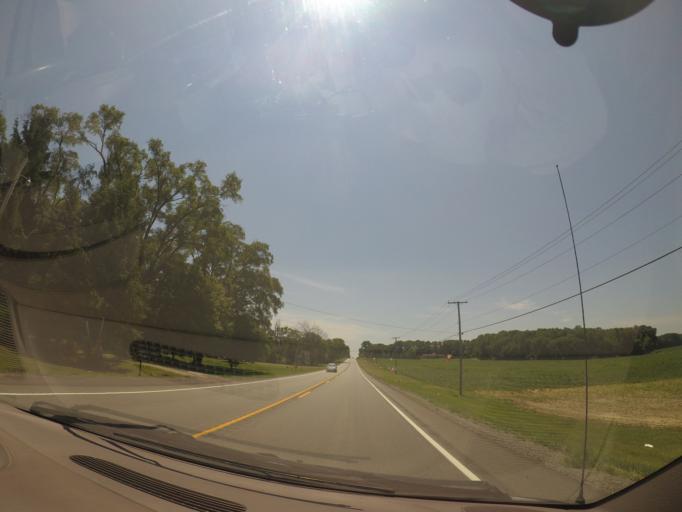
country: US
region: Indiana
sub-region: LaPorte County
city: Westville
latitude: 41.6218
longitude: -86.8945
